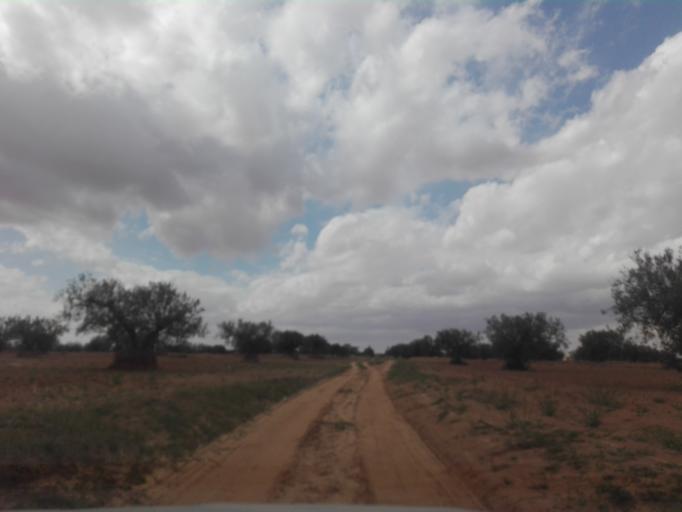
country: TN
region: Safaqis
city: Sfax
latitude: 34.6926
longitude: 10.4491
